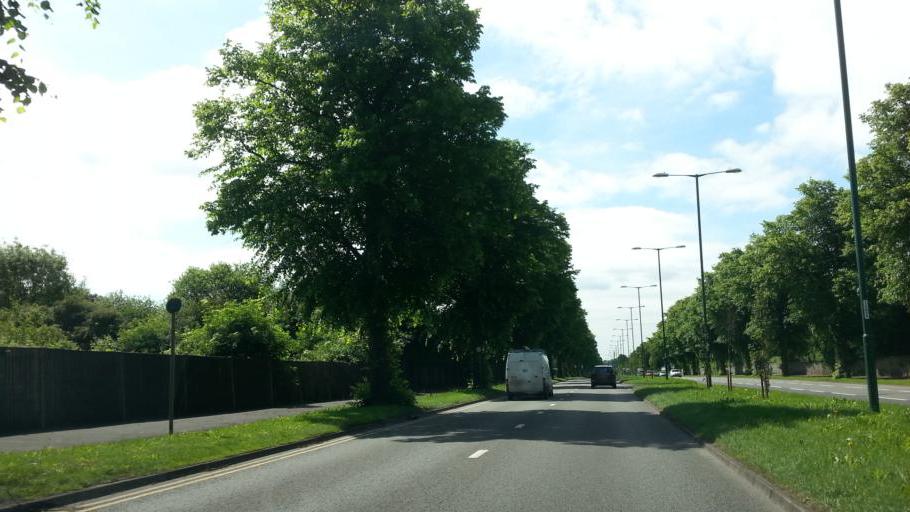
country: GB
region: England
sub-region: Nottingham
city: Nottingham
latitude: 52.9659
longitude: -1.1907
